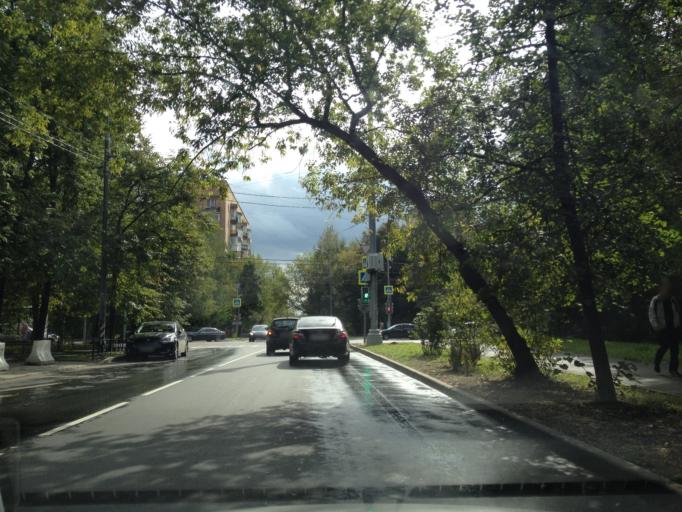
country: RU
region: Moskovskaya
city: Izmaylovo
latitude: 55.7937
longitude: 37.7940
